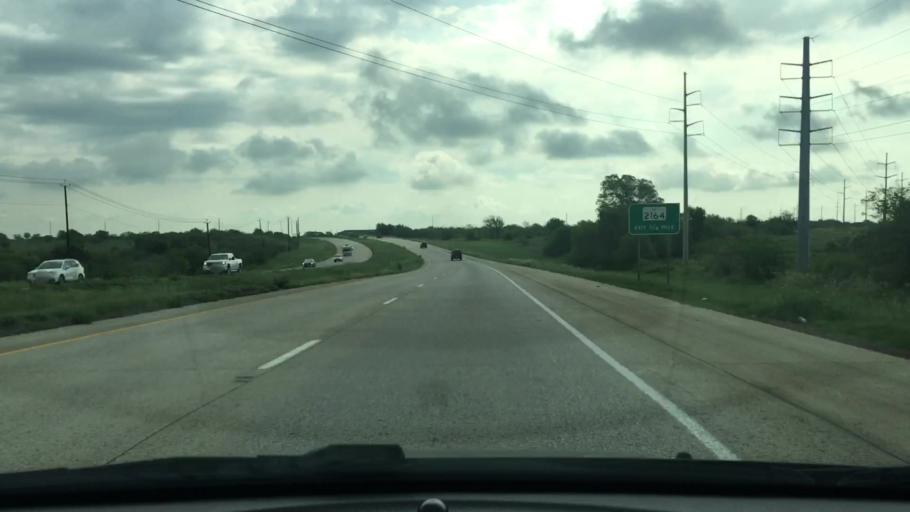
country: US
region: Texas
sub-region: Denton County
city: Denton
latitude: 33.2577
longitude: -97.1498
